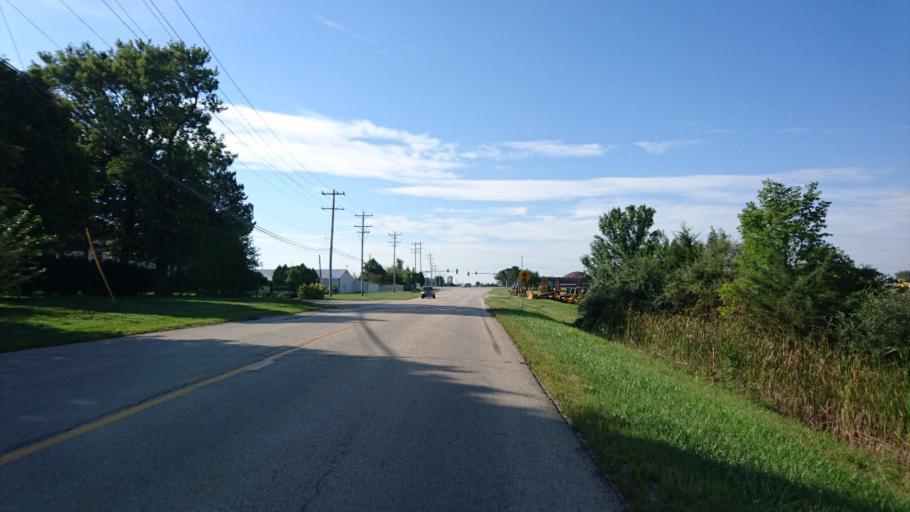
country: US
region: Illinois
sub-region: Will County
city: Ingalls Park
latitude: 41.4843
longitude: -88.0227
